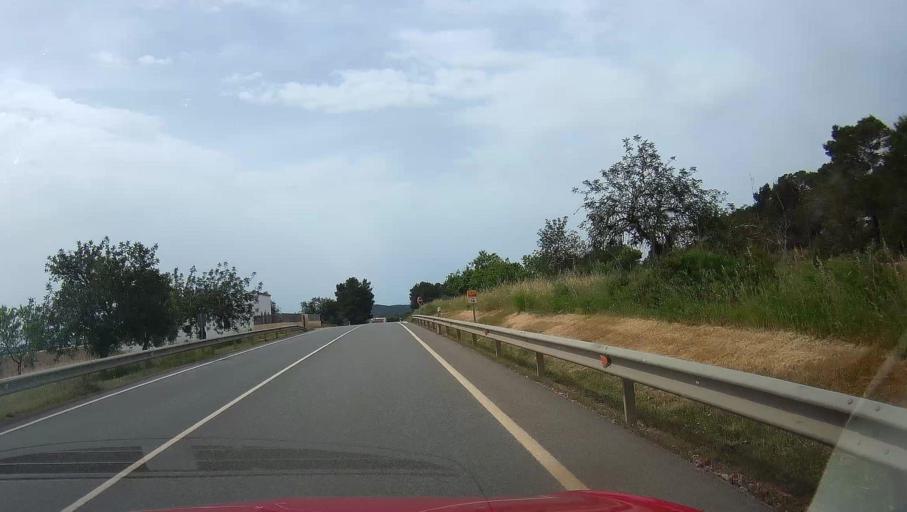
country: ES
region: Balearic Islands
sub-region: Illes Balears
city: Sant Joan de Labritja
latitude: 39.0377
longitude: 1.4914
